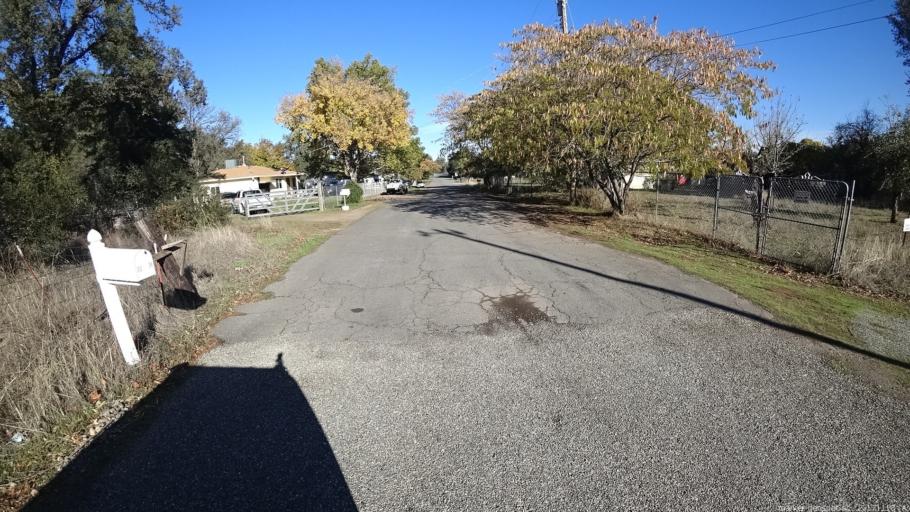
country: US
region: California
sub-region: Shasta County
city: Cottonwood
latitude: 40.3819
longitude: -122.3168
